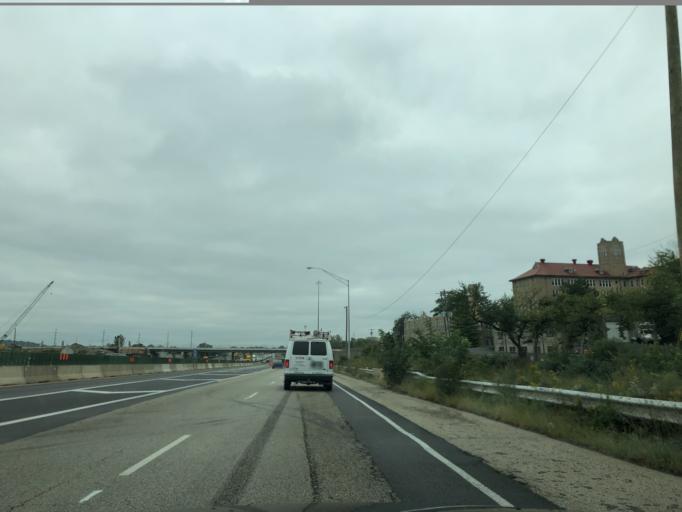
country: US
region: Ohio
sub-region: Hamilton County
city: Glendale
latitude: 39.2570
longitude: -84.4425
